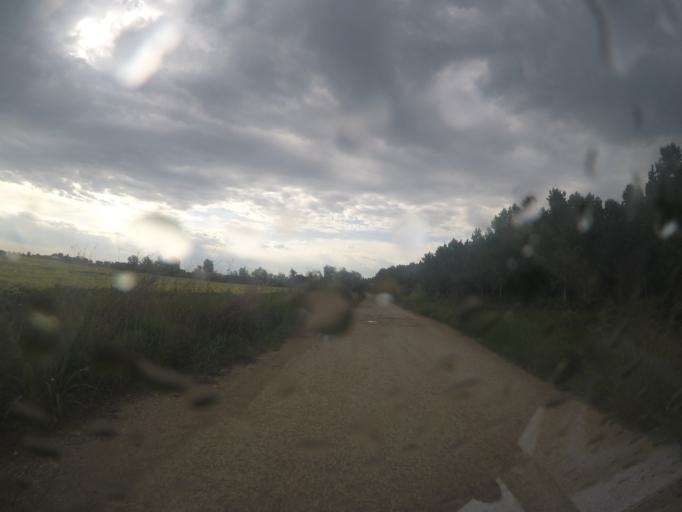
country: RS
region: Central Serbia
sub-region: Belgrade
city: Zemun
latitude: 44.8743
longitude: 20.3849
